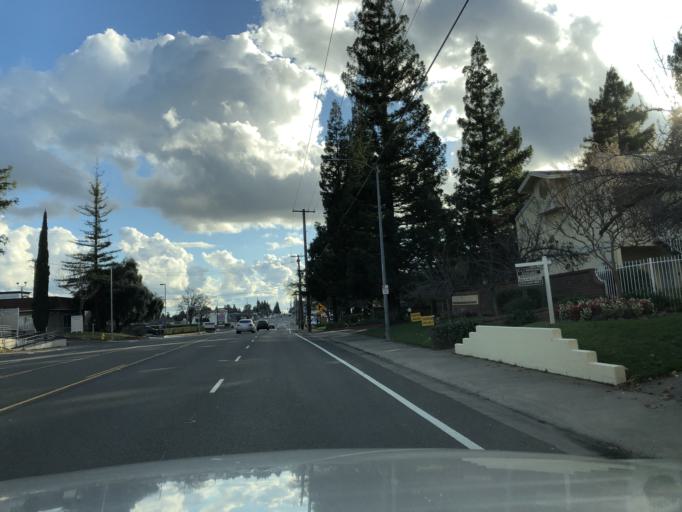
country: US
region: California
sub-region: Sacramento County
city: Foothill Farms
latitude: 38.6530
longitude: -121.3278
